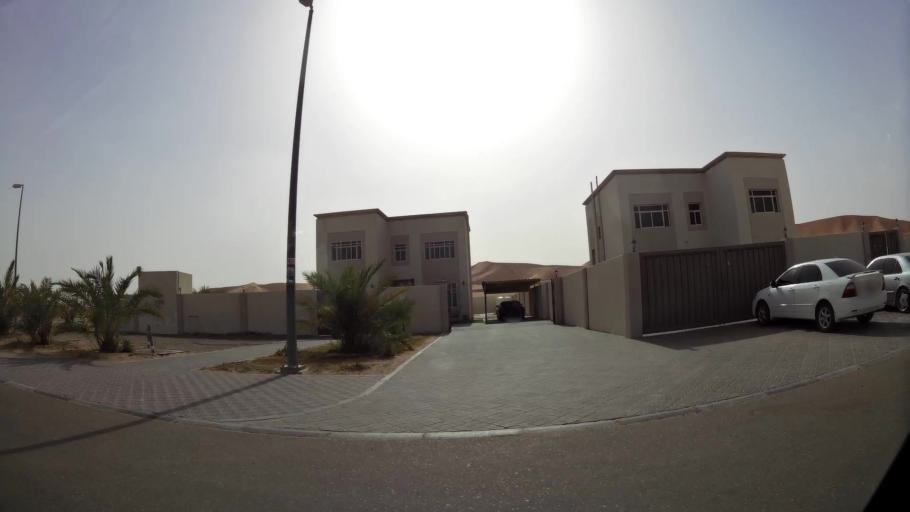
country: AE
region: Abu Dhabi
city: Al Ain
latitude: 24.2181
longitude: 55.5835
